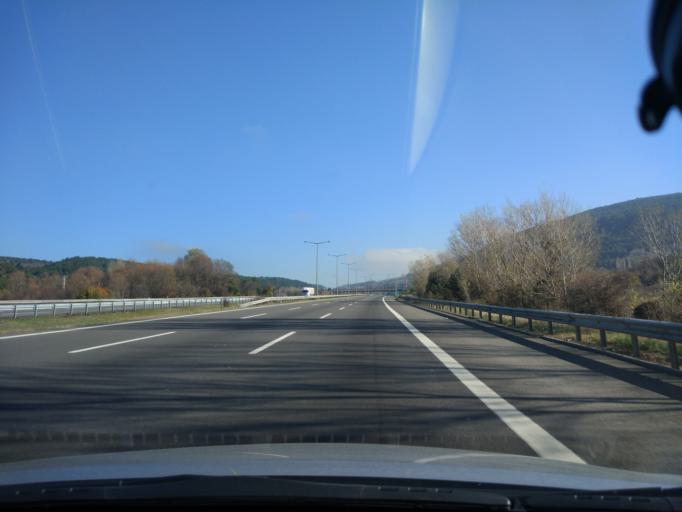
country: TR
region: Bolu
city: Yenicaga
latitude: 40.7423
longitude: 31.8511
